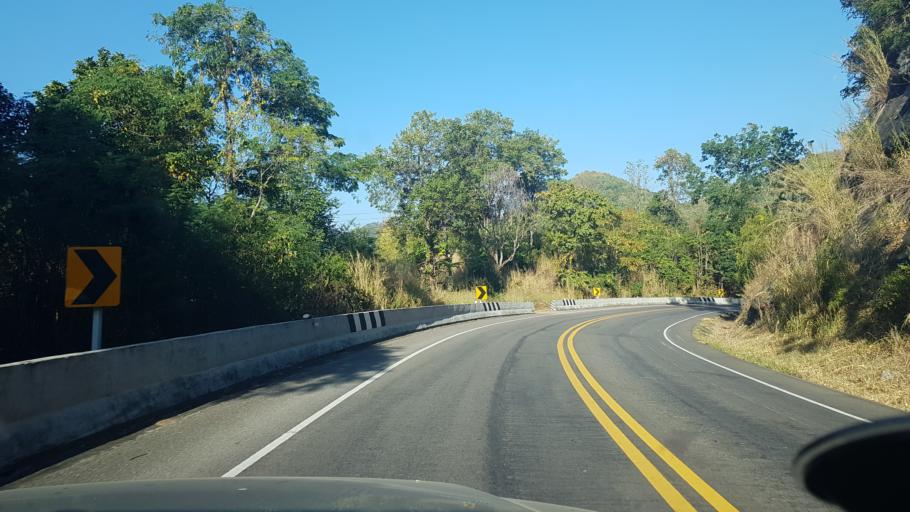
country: TH
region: Phetchabun
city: Lom Sak
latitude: 16.7439
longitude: 101.4010
